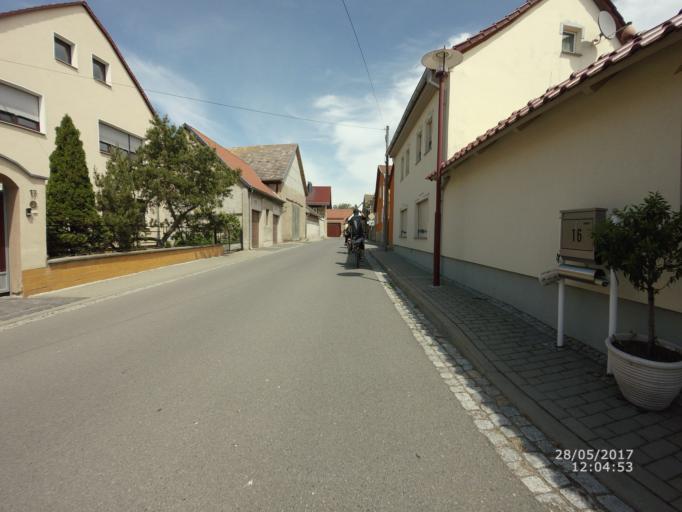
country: DE
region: Thuringia
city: Buchel
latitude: 51.2472
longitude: 11.1551
